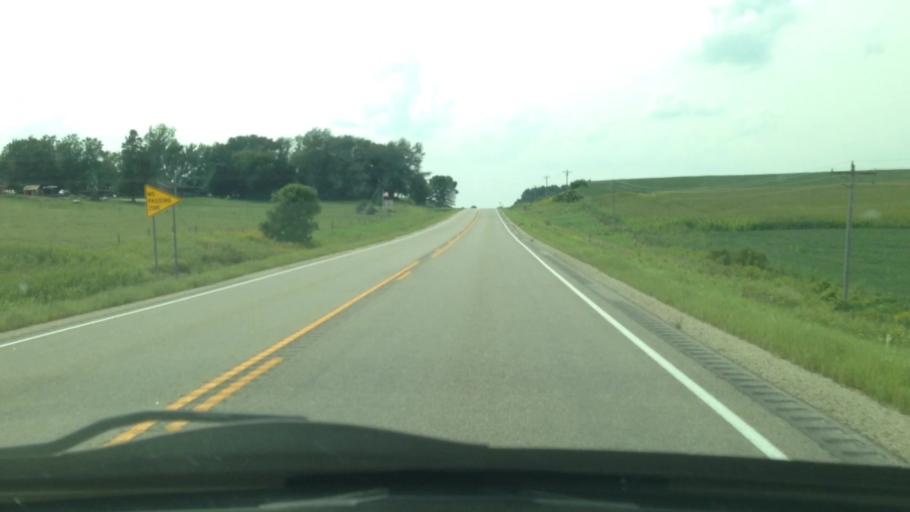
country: US
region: Minnesota
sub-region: Wabasha County
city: Elgin
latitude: 44.1653
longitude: -92.2214
